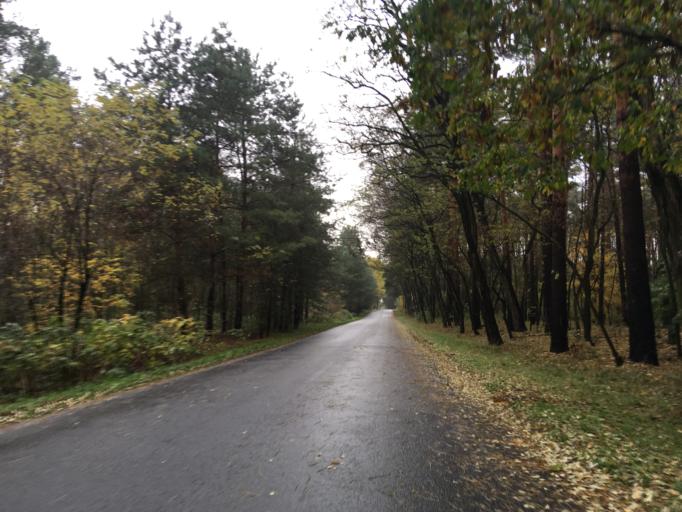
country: DE
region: Brandenburg
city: Friedland
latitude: 52.0507
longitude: 14.1876
